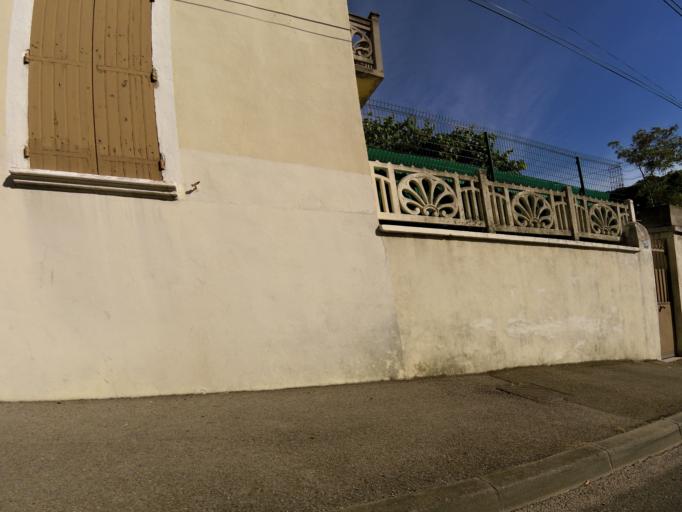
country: FR
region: Languedoc-Roussillon
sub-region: Departement du Gard
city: Nimes
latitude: 43.8424
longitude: 4.3420
